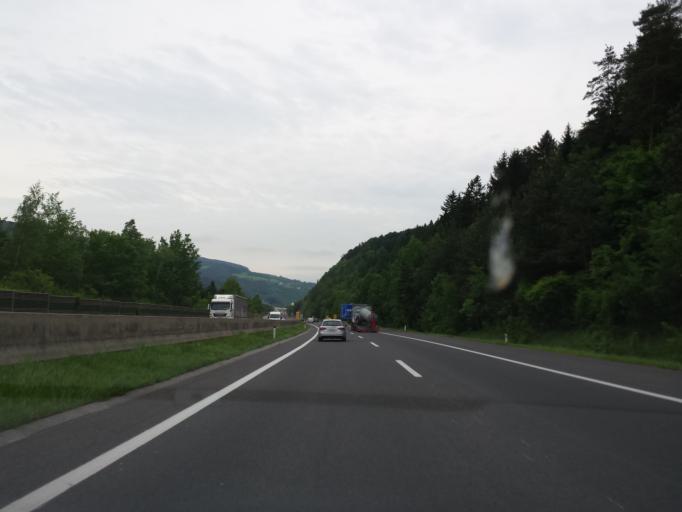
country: AT
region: Lower Austria
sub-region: Politischer Bezirk Neunkirchen
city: Warth
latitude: 47.6457
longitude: 16.1232
